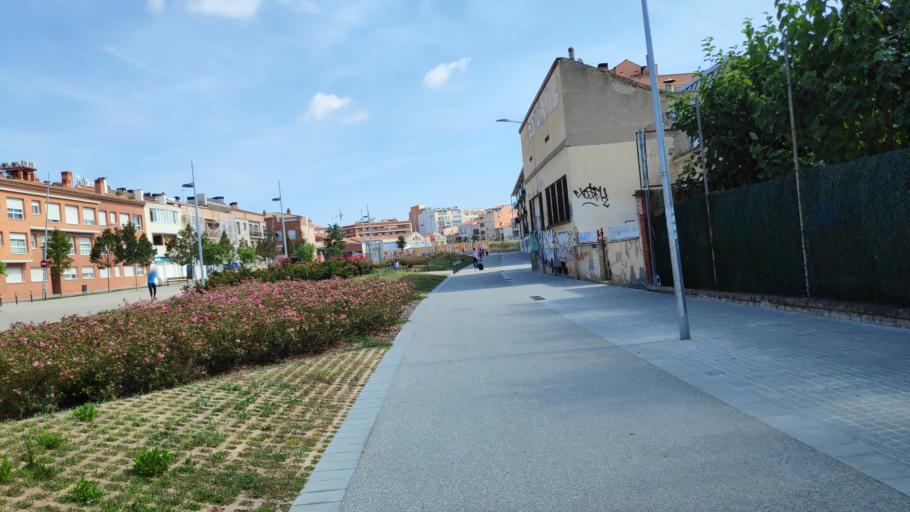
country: ES
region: Catalonia
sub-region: Provincia de Barcelona
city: Sabadell
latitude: 41.5422
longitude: 2.0997
